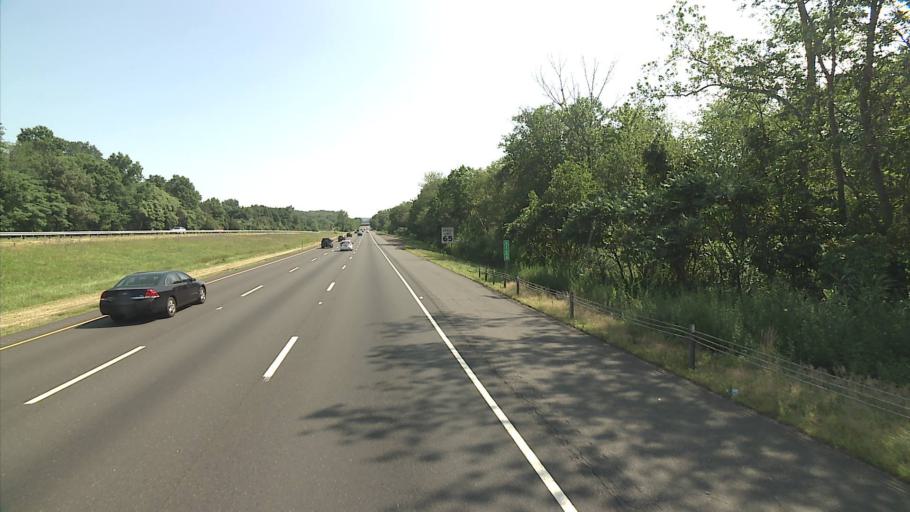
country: US
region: Connecticut
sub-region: New Haven County
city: Wallingford Center
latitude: 41.4388
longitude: -72.7960
